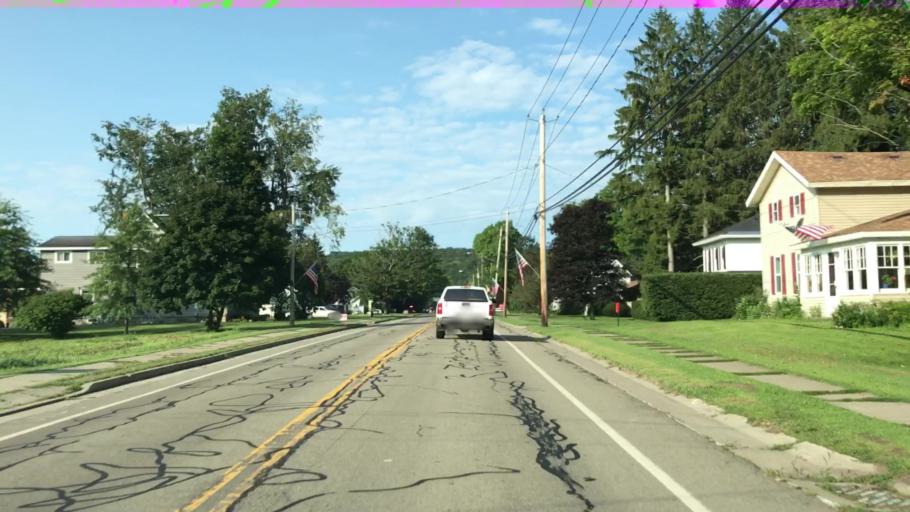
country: US
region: New York
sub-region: Chautauqua County
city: Fredonia
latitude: 42.3408
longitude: -79.3155
